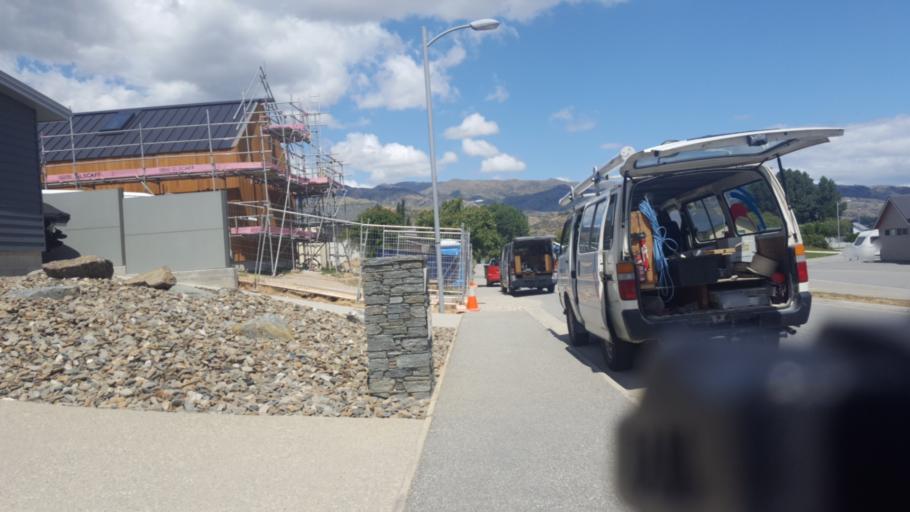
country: NZ
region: Otago
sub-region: Queenstown-Lakes District
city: Wanaka
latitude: -44.9794
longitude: 169.2373
